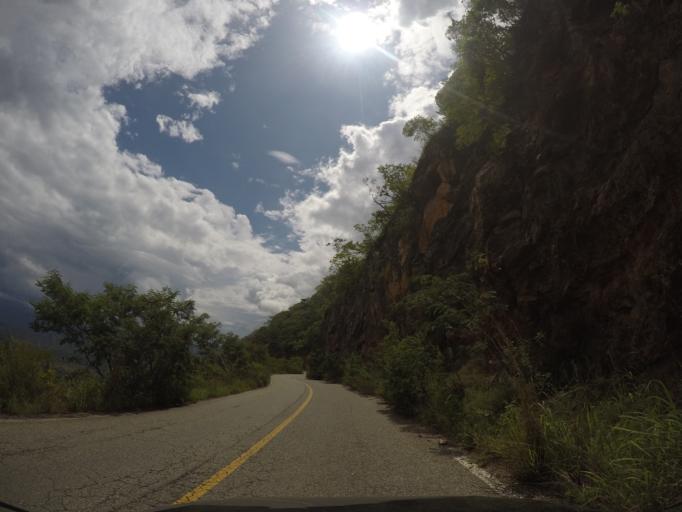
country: MX
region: Oaxaca
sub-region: San Jeronimo Coatlan
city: San Cristobal Honduras
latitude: 16.4318
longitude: -97.0420
